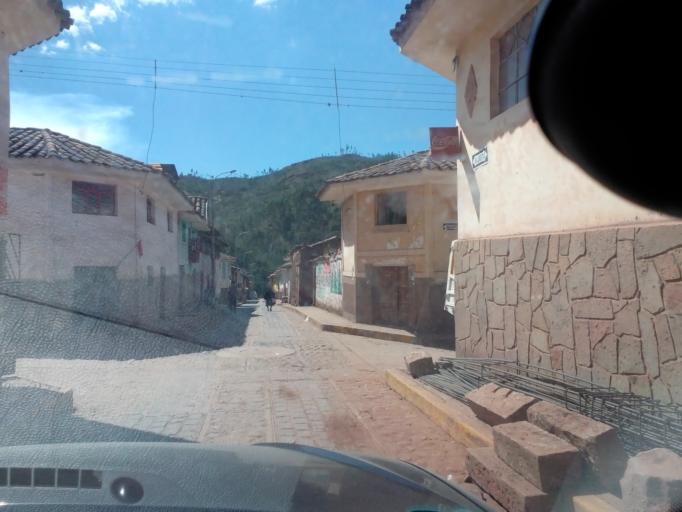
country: PE
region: Cusco
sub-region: Provincia de Anta
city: Huarocondo
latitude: -13.4142
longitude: -72.2076
